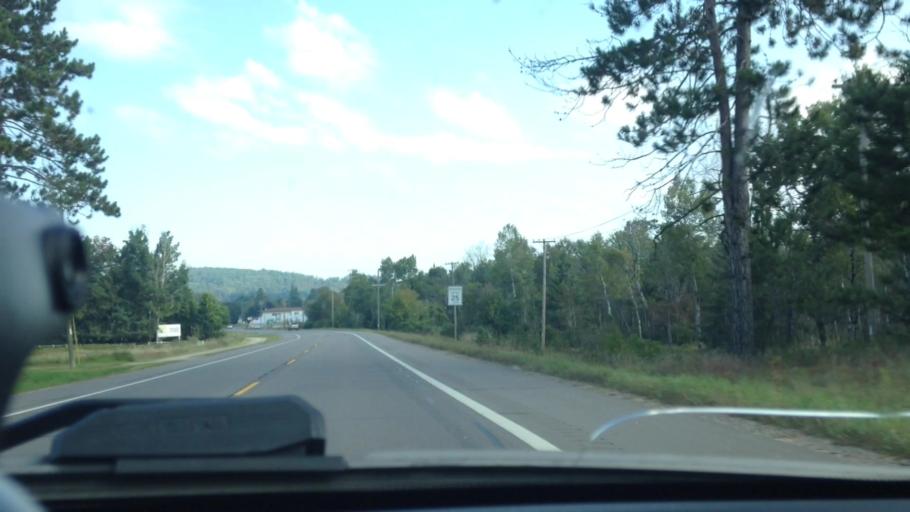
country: US
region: Michigan
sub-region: Dickinson County
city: Norway
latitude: 45.7768
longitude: -87.9090
